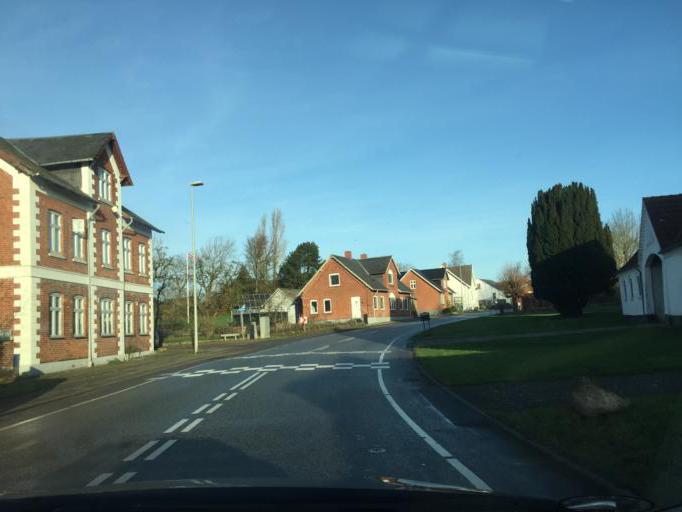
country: DK
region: South Denmark
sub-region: Middelfart Kommune
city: Ejby
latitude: 55.4372
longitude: 9.9420
